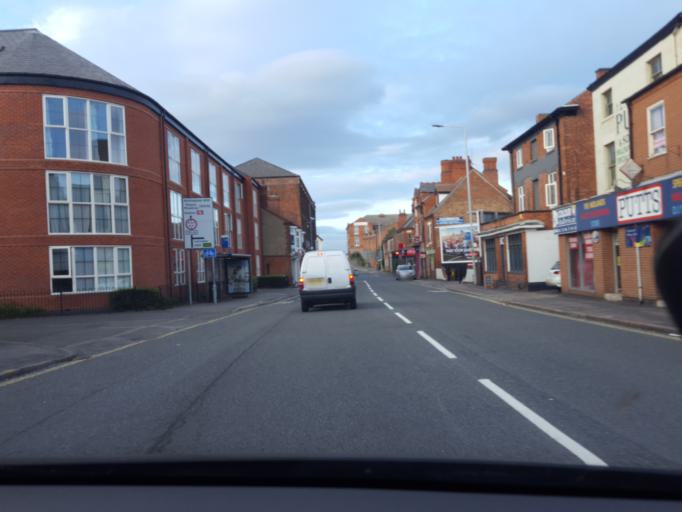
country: GB
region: England
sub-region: Leicestershire
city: Loughborough
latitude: 52.7752
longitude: -1.2002
